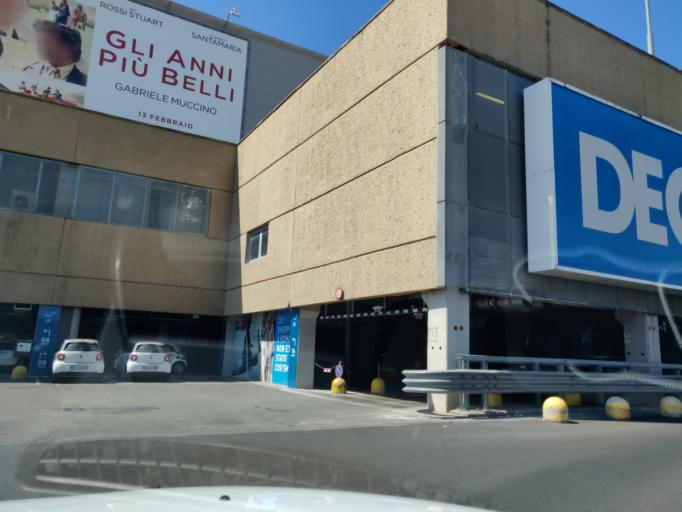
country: IT
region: Latium
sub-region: Citta metropolitana di Roma Capitale
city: Colle Verde
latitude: 41.9716
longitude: 12.5421
